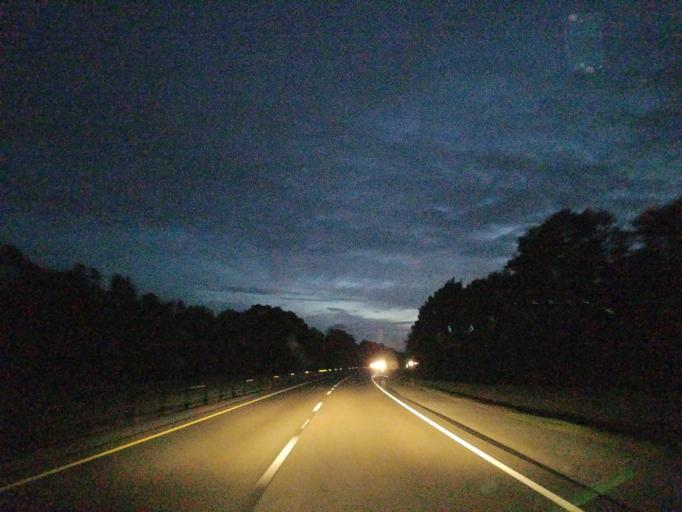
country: US
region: Mississippi
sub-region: Jones County
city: Laurel
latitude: 31.7194
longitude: -89.1052
